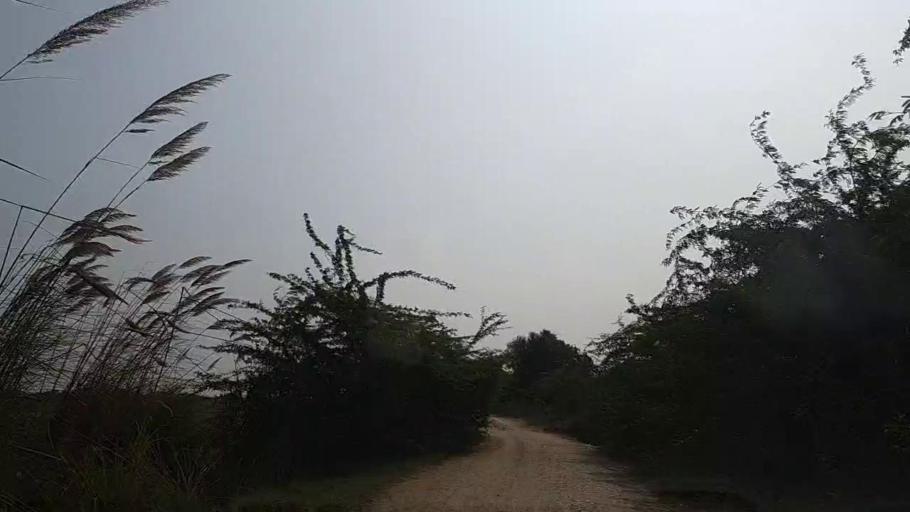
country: PK
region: Sindh
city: Mirpur Sakro
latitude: 24.5953
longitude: 67.7172
